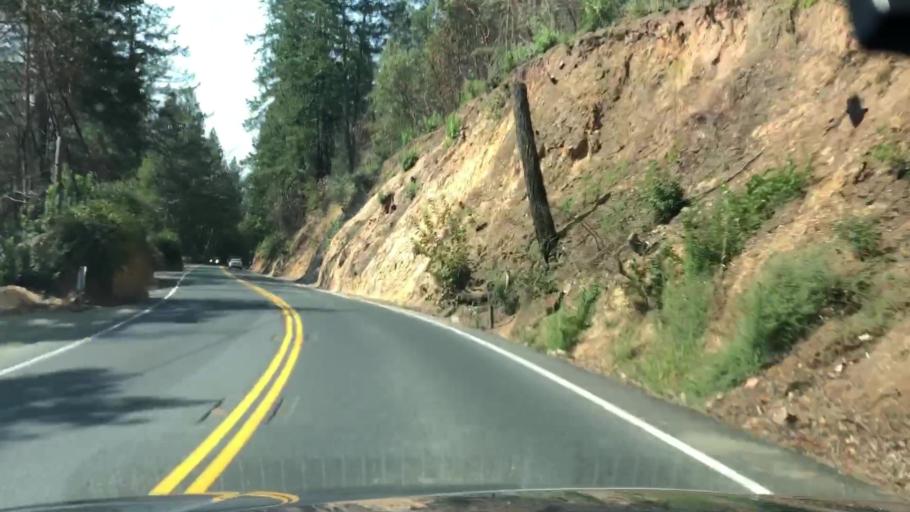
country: US
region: California
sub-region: Napa County
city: Calistoga
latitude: 38.6395
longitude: -122.5999
